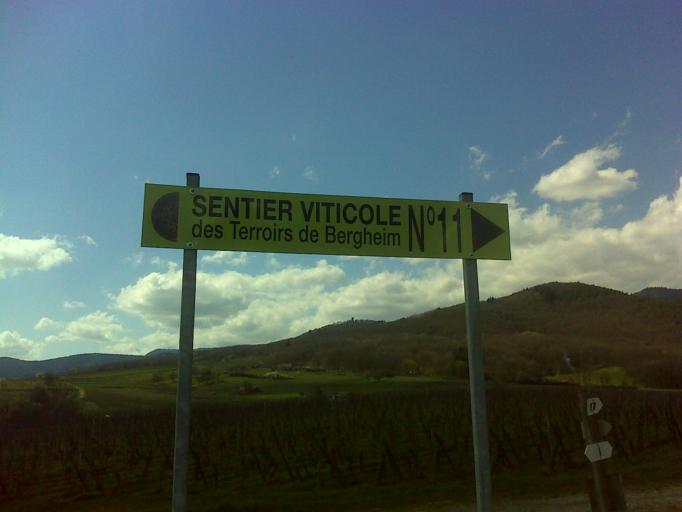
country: FR
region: Alsace
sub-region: Departement du Haut-Rhin
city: Bergheim
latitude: 48.2102
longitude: 7.3482
